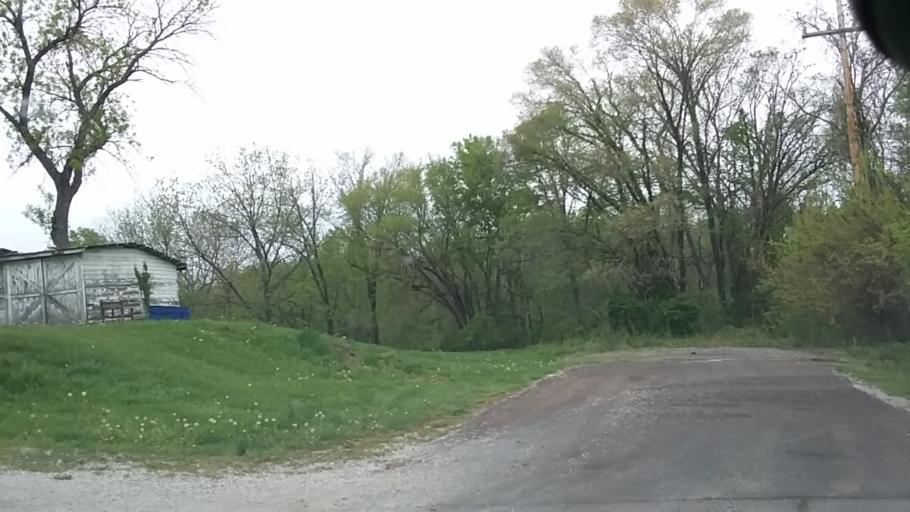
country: US
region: Kansas
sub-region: Douglas County
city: Eudora
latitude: 38.9493
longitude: -95.0940
